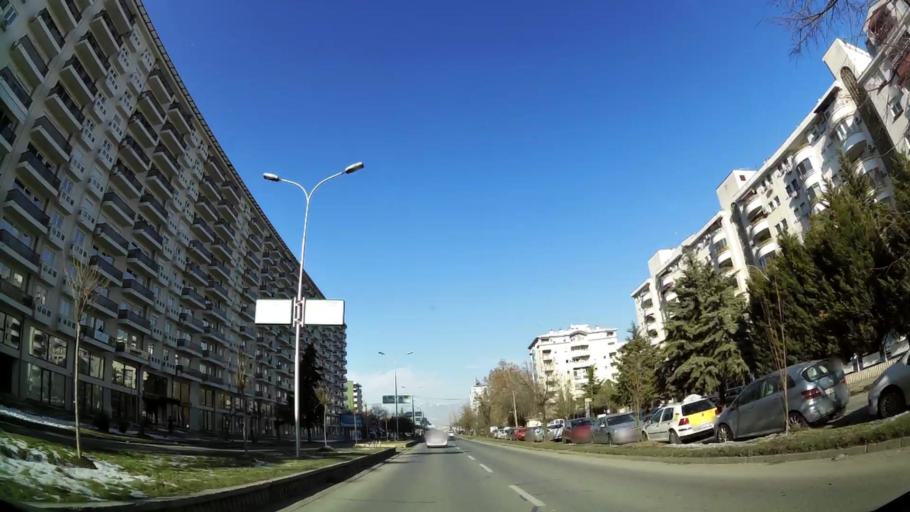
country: MK
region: Karpos
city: Skopje
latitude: 41.9985
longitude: 21.4040
